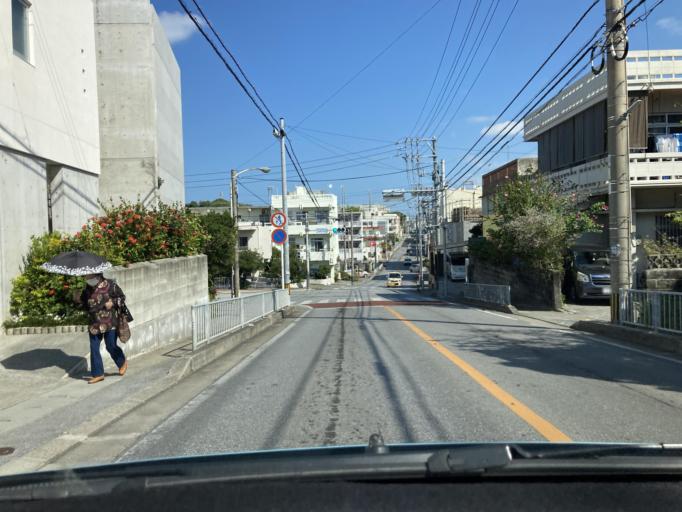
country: JP
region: Okinawa
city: Tomigusuku
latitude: 26.1859
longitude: 127.6665
